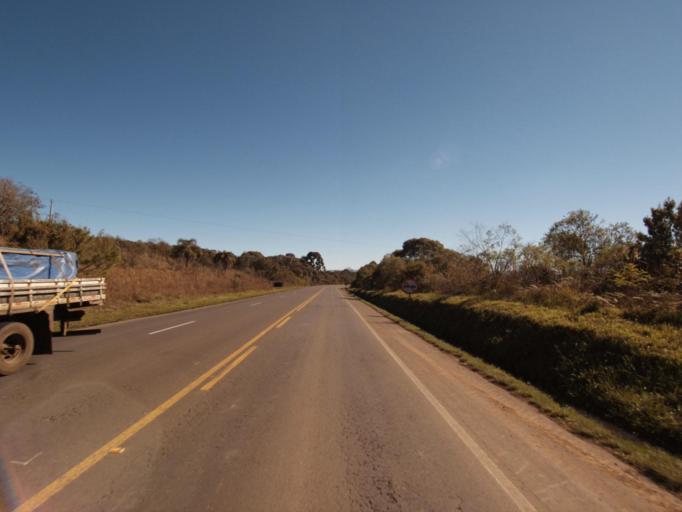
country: BR
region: Santa Catarina
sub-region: Joacaba
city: Joacaba
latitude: -27.0938
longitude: -51.6582
